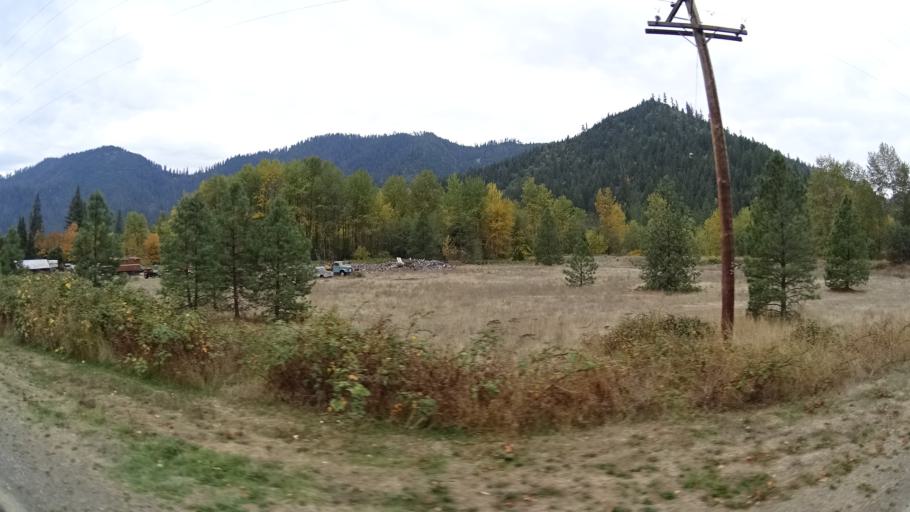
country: US
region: California
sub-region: Siskiyou County
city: Happy Camp
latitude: 41.8687
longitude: -123.4045
